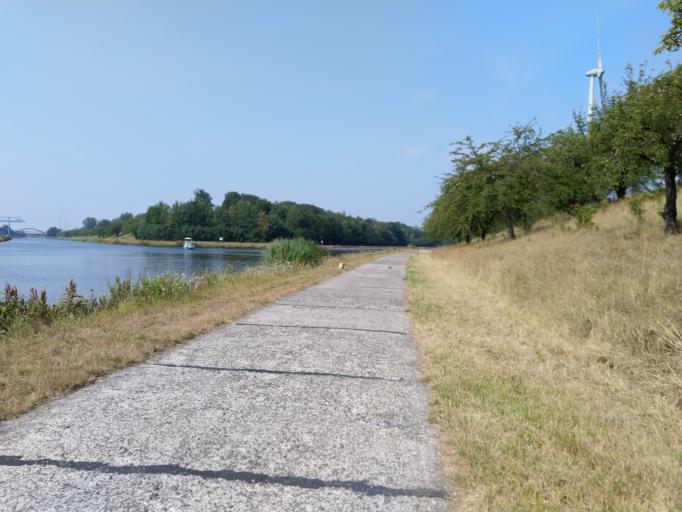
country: BE
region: Wallonia
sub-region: Province du Hainaut
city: La Louviere
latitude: 50.4997
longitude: 4.1939
